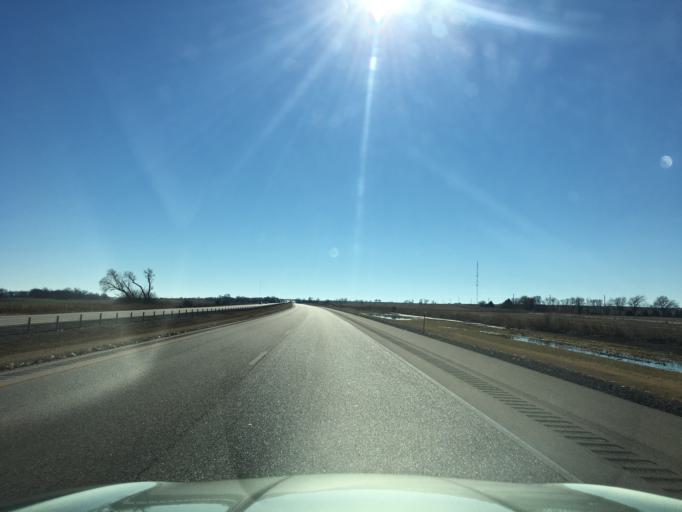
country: US
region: Oklahoma
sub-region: Kay County
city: Blackwell
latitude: 36.8944
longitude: -97.3540
